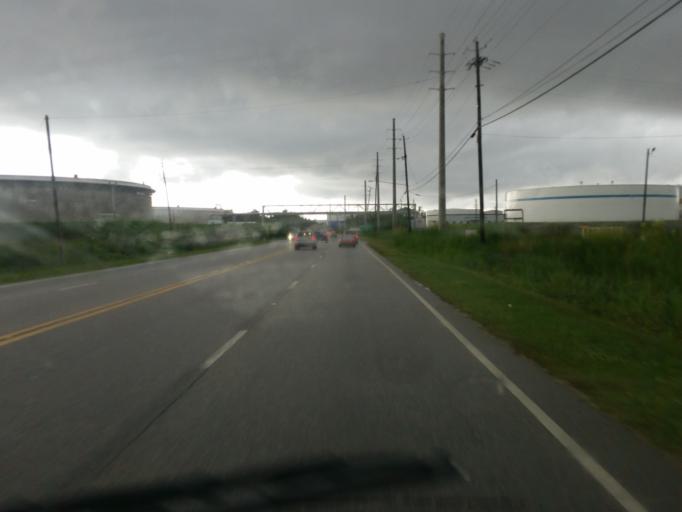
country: US
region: Alabama
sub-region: Mobile County
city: Mobile
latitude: 30.6991
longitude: -88.0323
